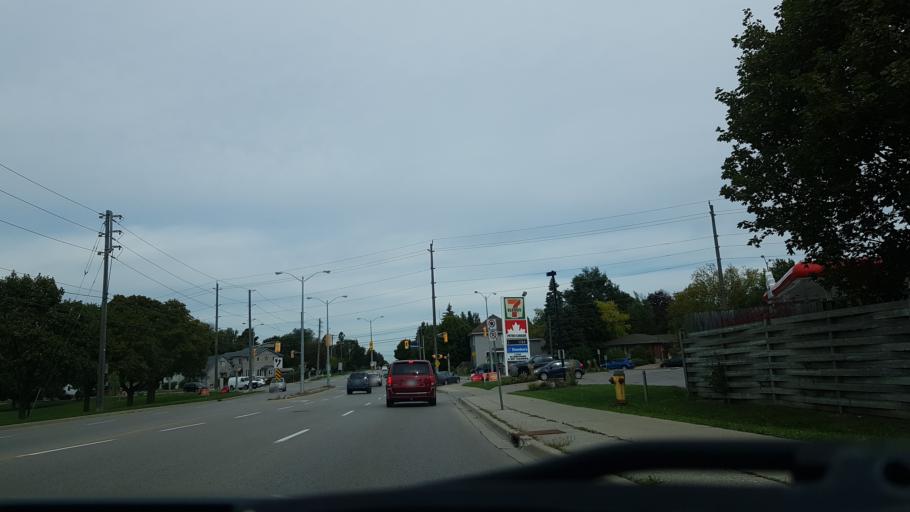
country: CA
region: Ontario
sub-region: Wellington County
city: Guelph
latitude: 43.5680
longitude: -80.2478
